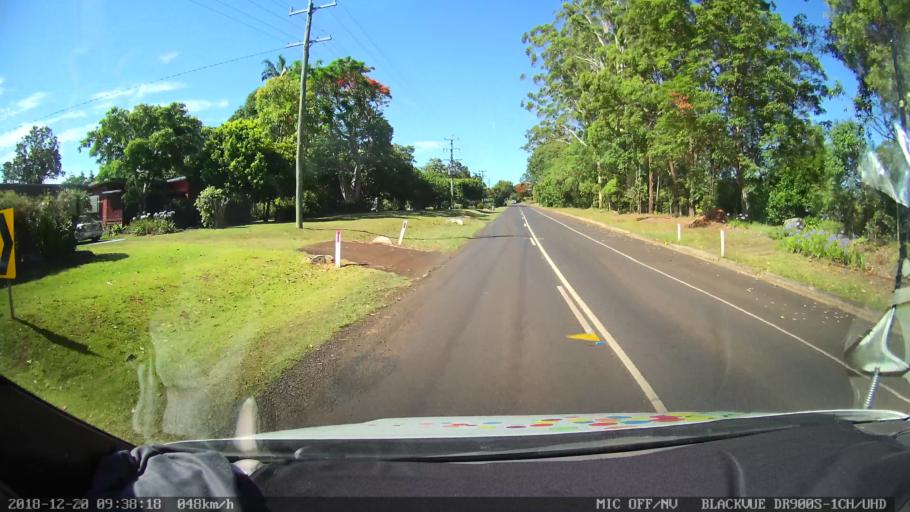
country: AU
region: New South Wales
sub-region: Lismore Municipality
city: Goonellabah
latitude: -28.6896
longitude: 153.3142
